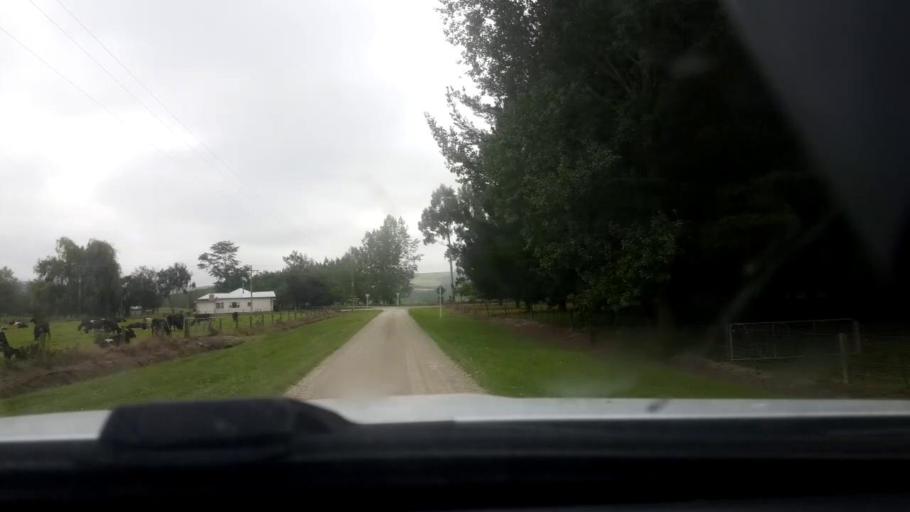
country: NZ
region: Canterbury
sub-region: Timaru District
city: Pleasant Point
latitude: -44.2081
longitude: 171.1127
